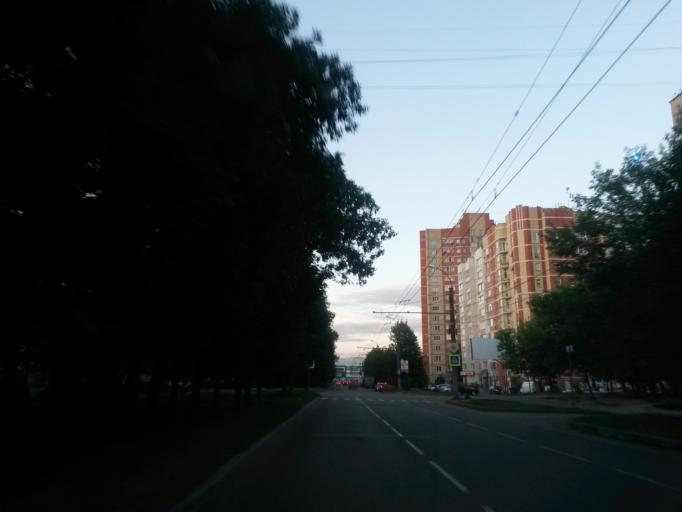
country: RU
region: Ivanovo
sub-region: Gorod Ivanovo
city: Ivanovo
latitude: 56.9639
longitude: 41.0182
